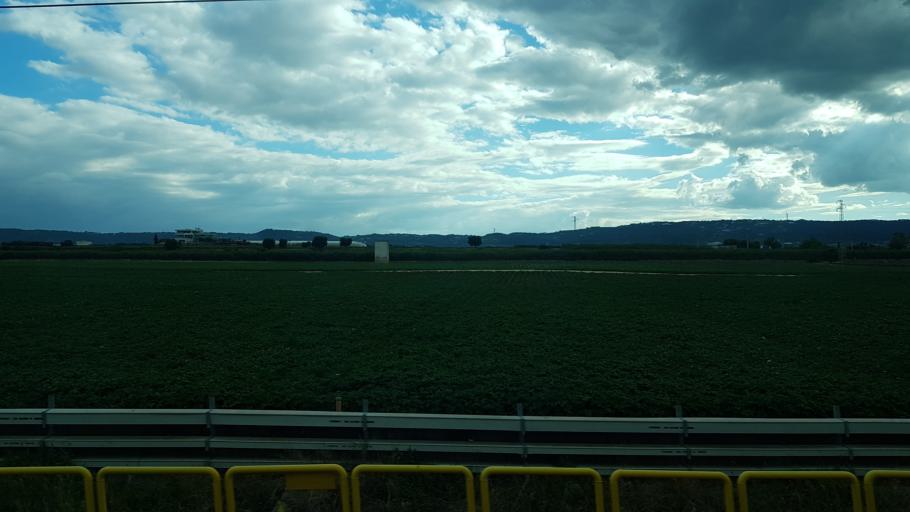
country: IT
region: Apulia
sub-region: Provincia di Brindisi
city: Fasano
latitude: 40.8479
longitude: 17.3914
